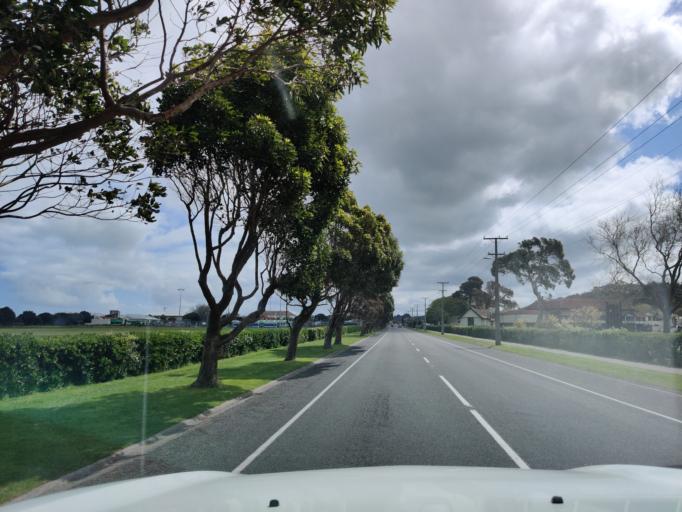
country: NZ
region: Manawatu-Wanganui
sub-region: Wanganui District
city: Wanganui
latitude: -39.9310
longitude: 175.0370
